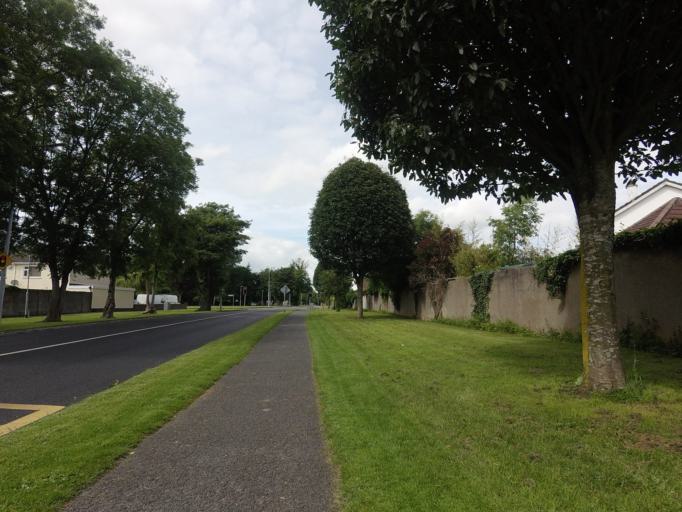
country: IE
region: Leinster
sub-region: Fingal County
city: Blanchardstown
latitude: 53.3791
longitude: -6.3923
